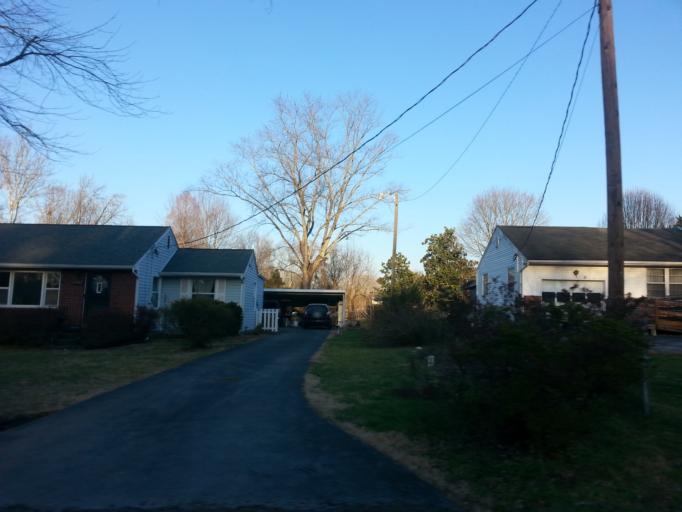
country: US
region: Tennessee
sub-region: Knox County
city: Knoxville
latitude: 36.0173
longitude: -83.8944
